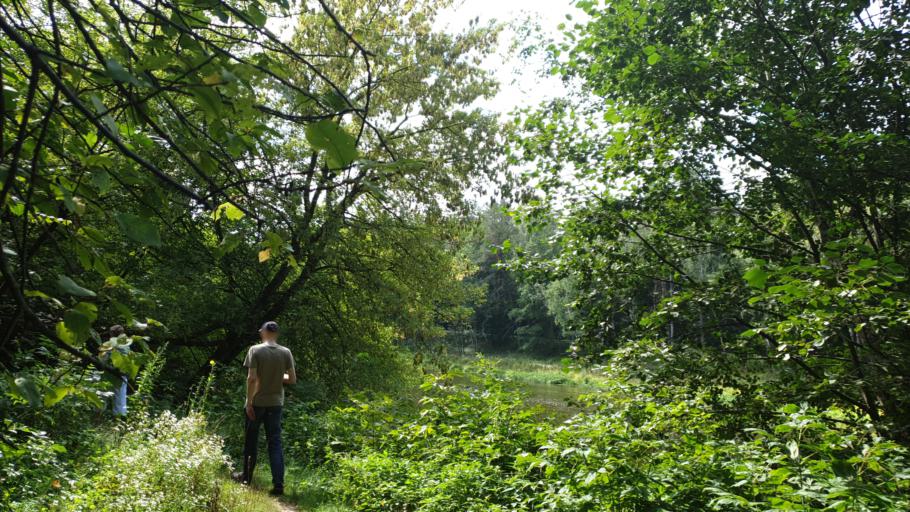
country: LT
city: Grigiskes
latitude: 54.8033
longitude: 24.9751
